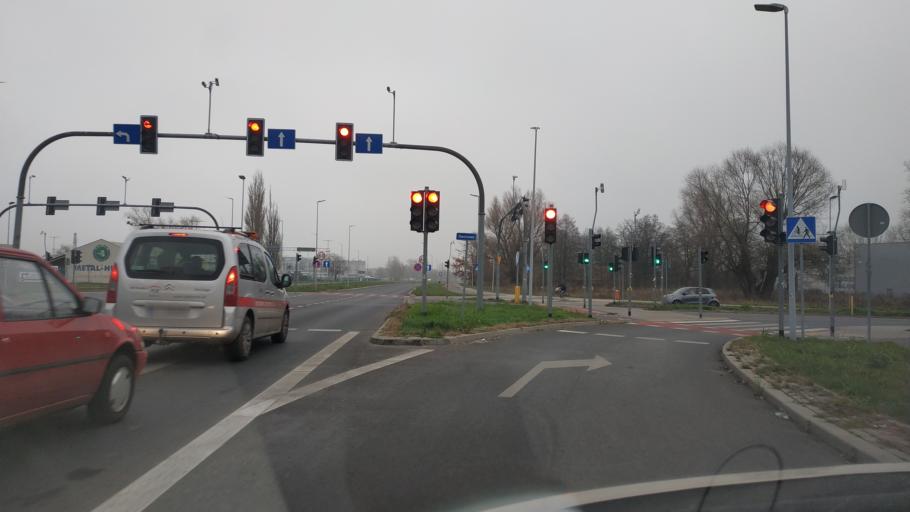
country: PL
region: Kujawsko-Pomorskie
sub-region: Torun
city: Torun
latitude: 53.0301
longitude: 18.6220
